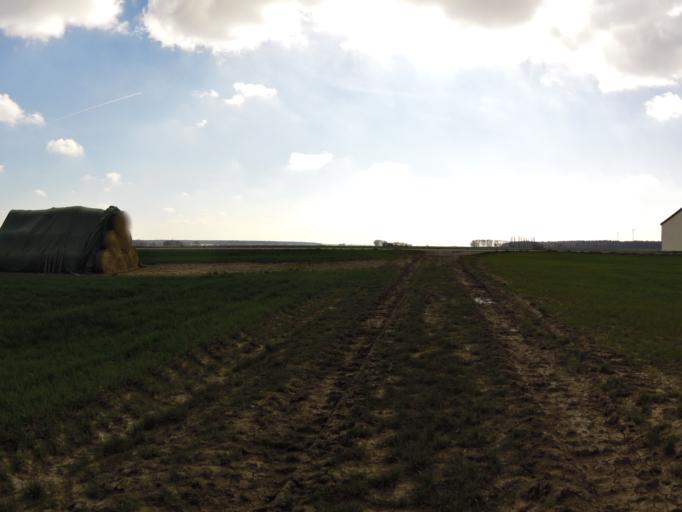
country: DE
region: Bavaria
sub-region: Regierungsbezirk Unterfranken
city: Biebelried
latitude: 49.7448
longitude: 10.0728
